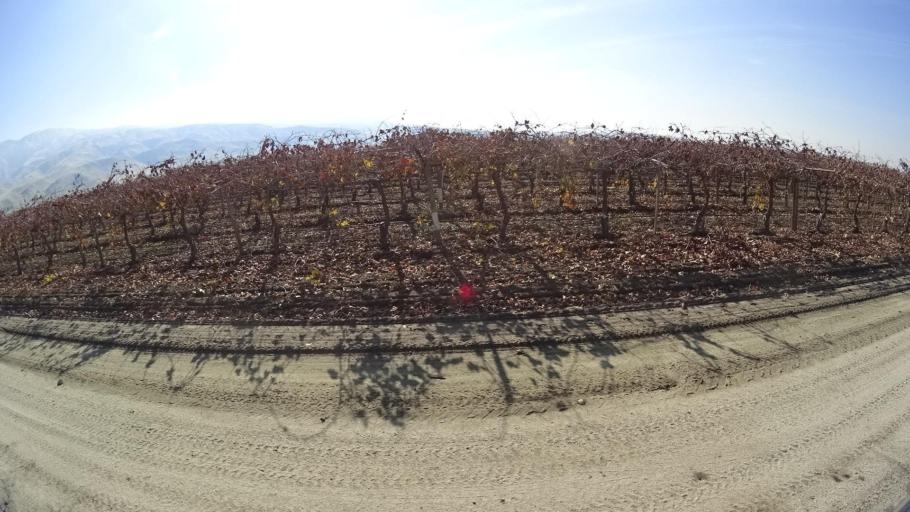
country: US
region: California
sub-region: Kern County
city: Arvin
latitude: 35.1947
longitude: -118.7893
